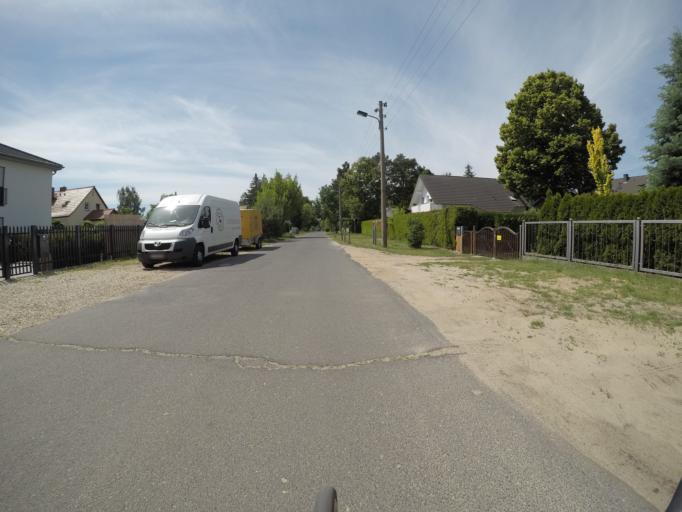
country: DE
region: Berlin
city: Mahlsdorf
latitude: 52.4851
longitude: 13.6162
